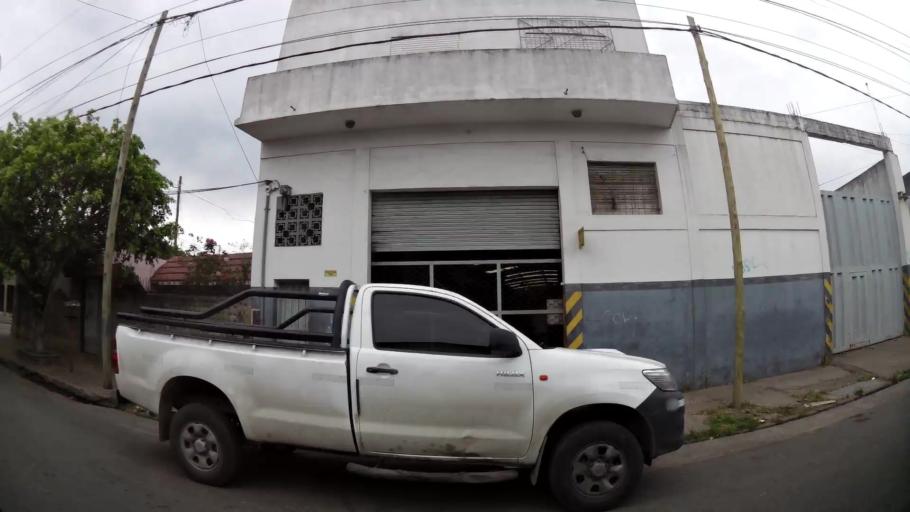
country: AR
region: Buenos Aires
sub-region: Partido de Avellaneda
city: Avellaneda
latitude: -34.6576
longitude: -58.3520
